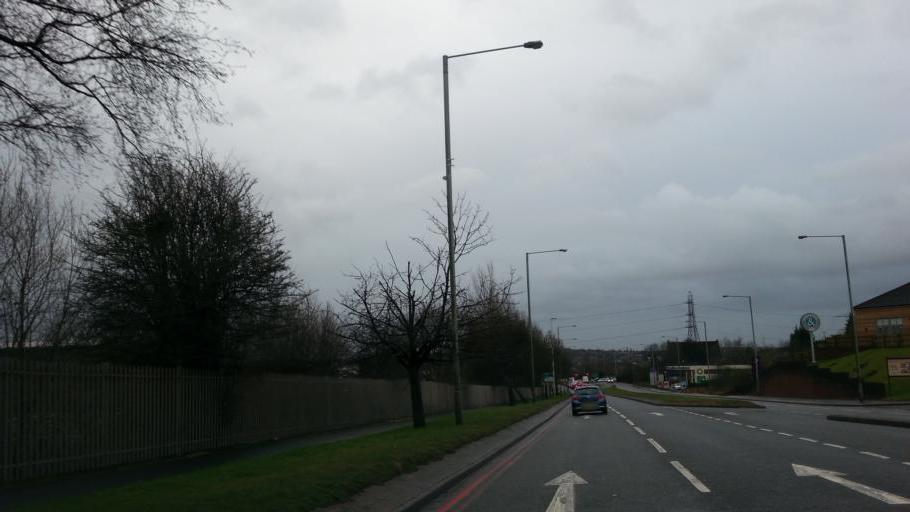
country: GB
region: England
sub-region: Sandwell
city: Oldbury
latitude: 52.5018
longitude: -2.0314
